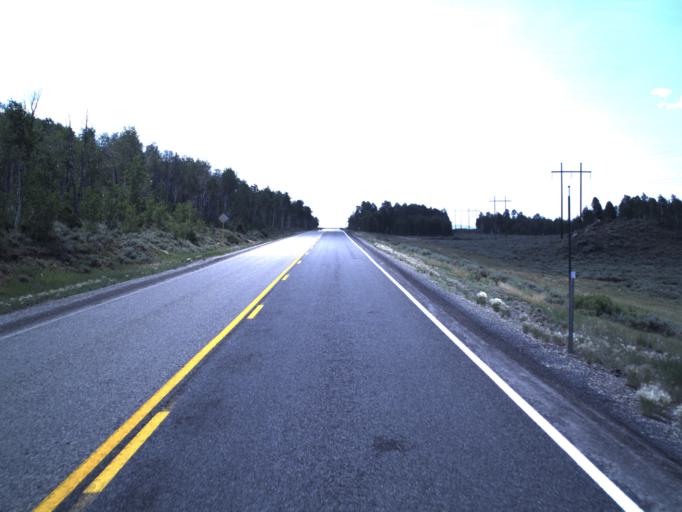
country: US
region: Utah
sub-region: Carbon County
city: Helper
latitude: 39.8604
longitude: -111.1244
